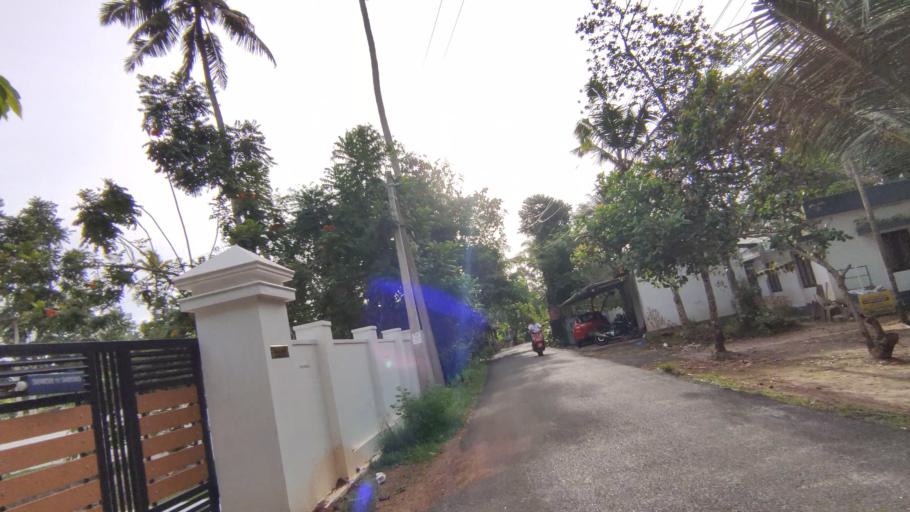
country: IN
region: Kerala
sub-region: Alappuzha
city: Shertallai
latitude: 9.6198
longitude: 76.3360
